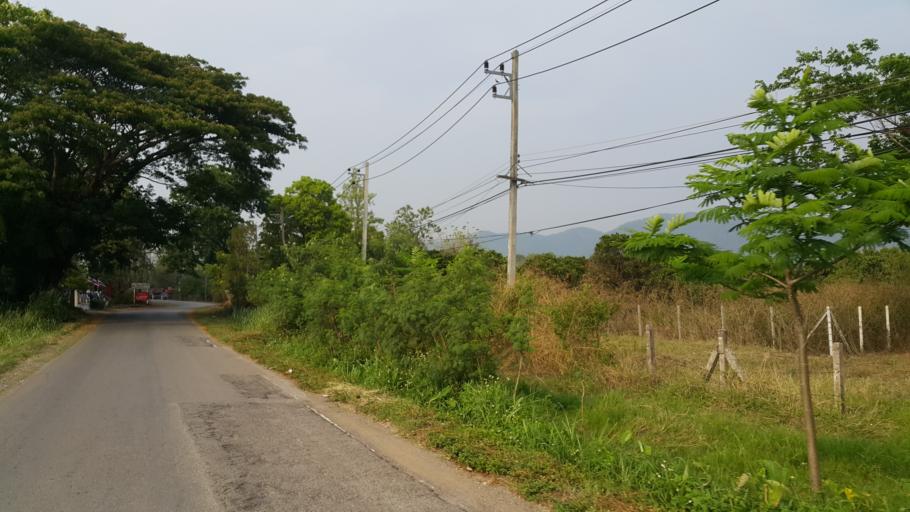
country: TH
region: Chiang Mai
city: Mae On
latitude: 18.7672
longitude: 99.2510
